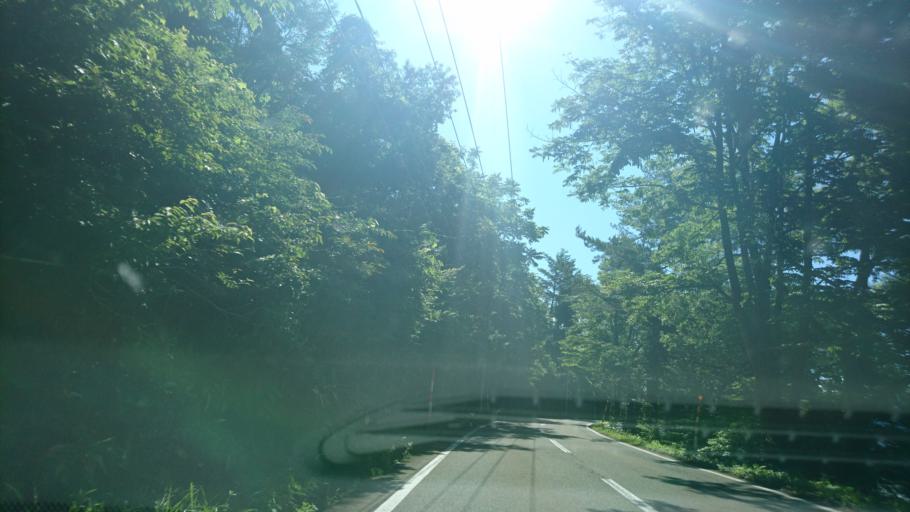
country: JP
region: Akita
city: Kakunodatemachi
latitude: 39.7507
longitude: 140.6576
